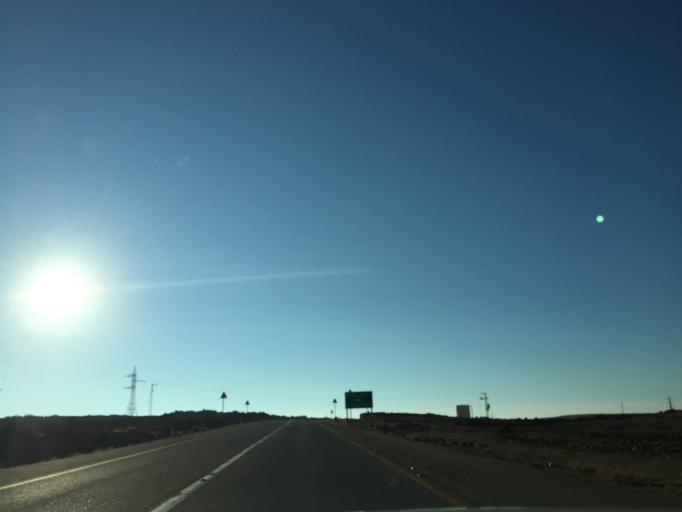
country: IL
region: Southern District
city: Mitzpe Ramon
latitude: 30.5201
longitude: 34.9399
